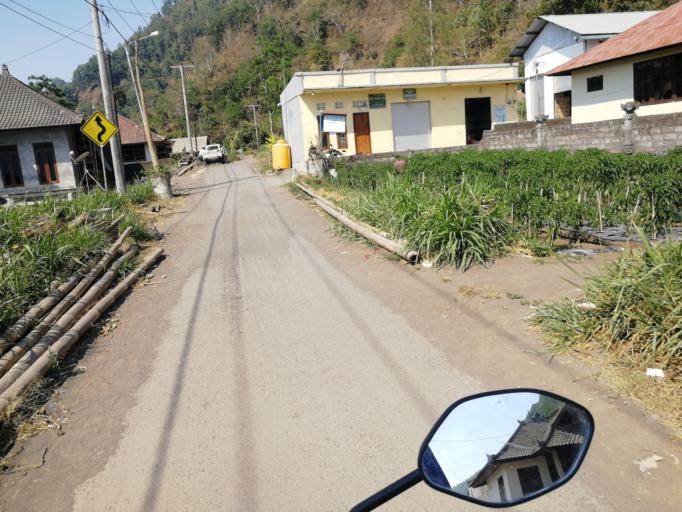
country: ID
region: Bali
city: Banjar Trunyan
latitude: -8.2643
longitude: 115.4209
